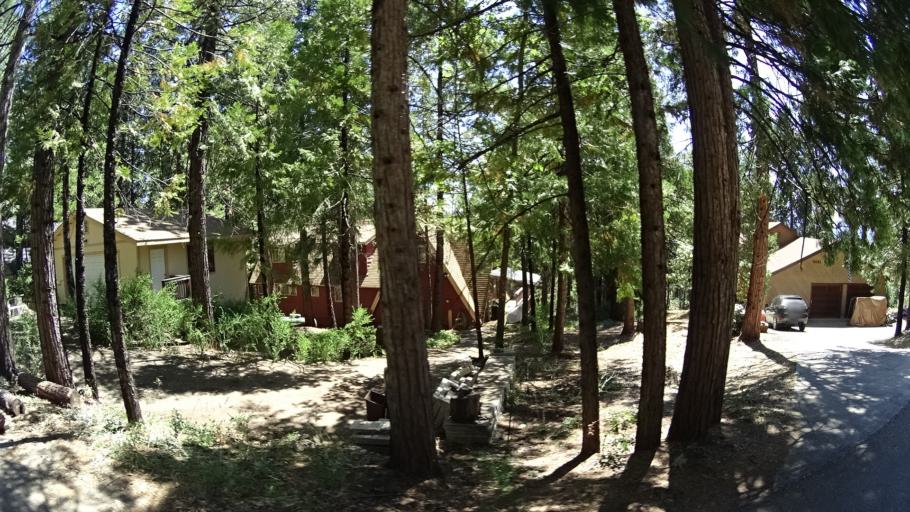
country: US
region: California
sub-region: Calaveras County
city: Arnold
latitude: 38.2298
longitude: -120.3728
